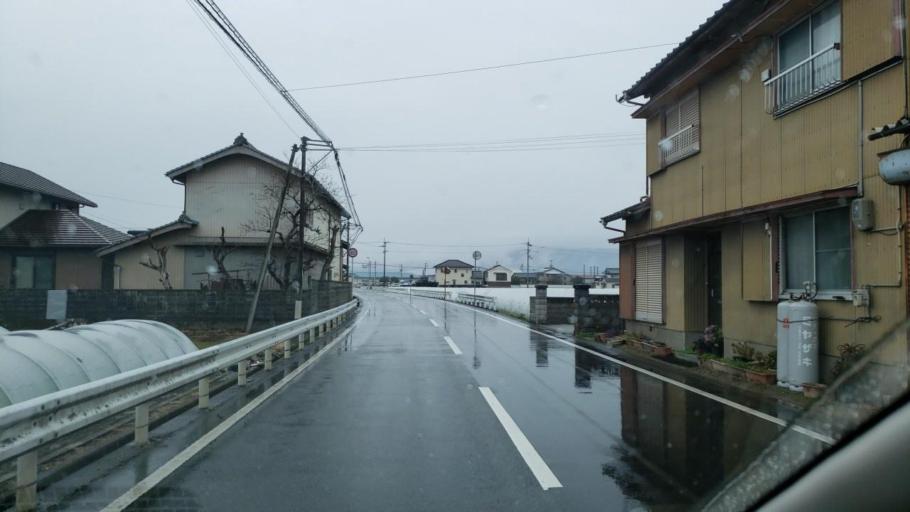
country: JP
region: Tokushima
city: Ishii
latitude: 34.1012
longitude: 134.4069
